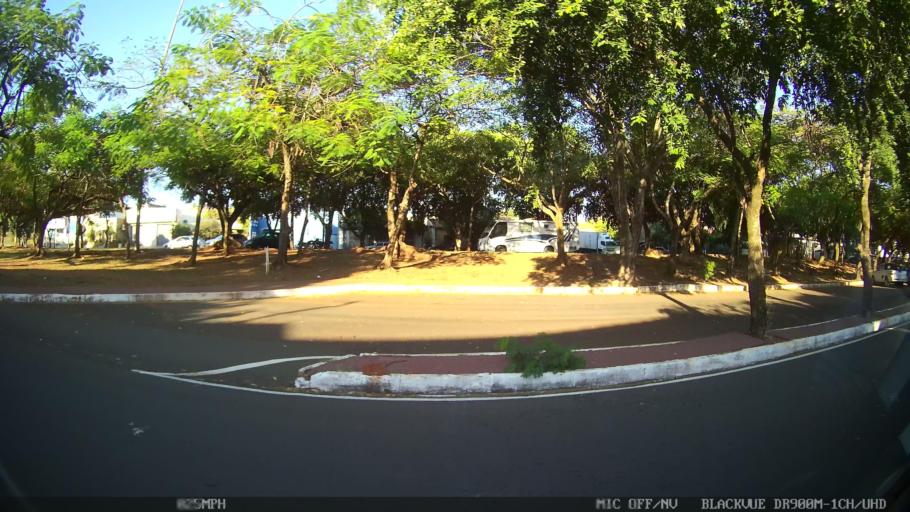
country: BR
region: Sao Paulo
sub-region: Sao Jose Do Rio Preto
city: Sao Jose do Rio Preto
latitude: -20.8016
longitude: -49.3597
